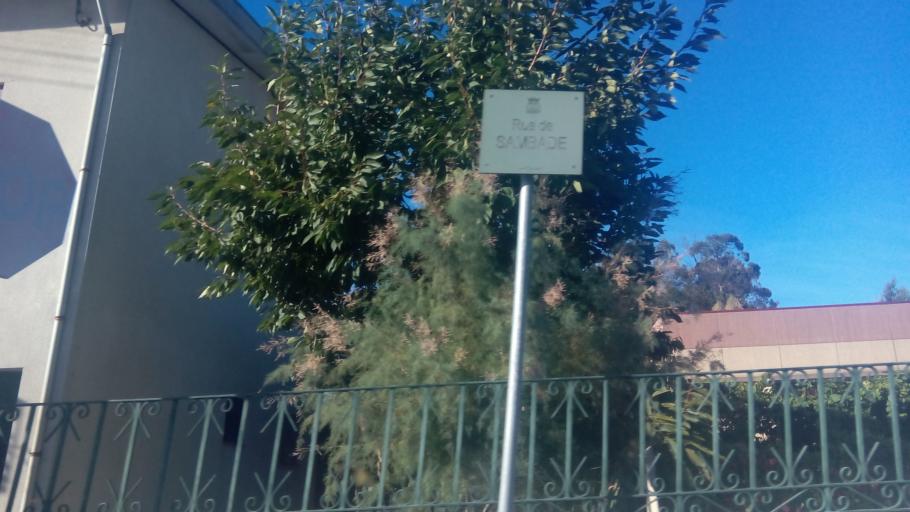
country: PT
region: Porto
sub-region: Paredes
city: Casteloes de Cepeda
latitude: 41.1935
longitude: -8.3428
